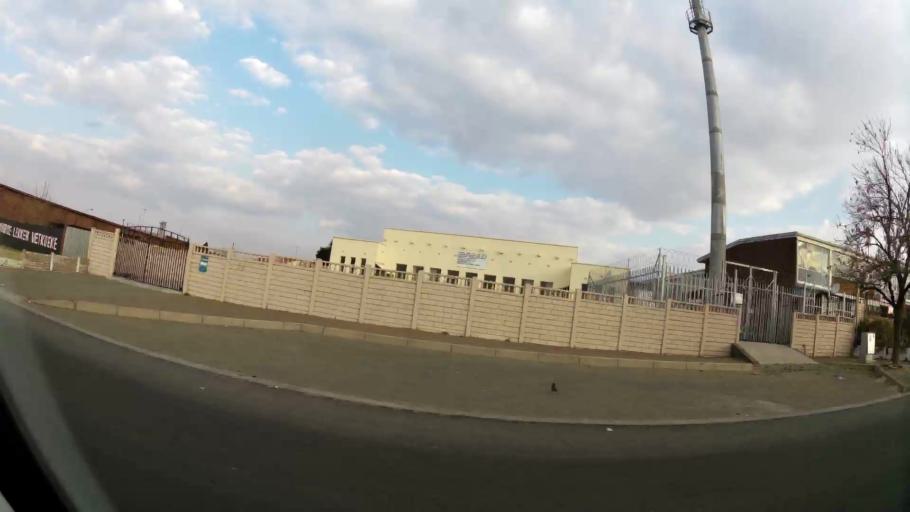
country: ZA
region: Gauteng
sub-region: Ekurhuleni Metropolitan Municipality
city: Germiston
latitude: -26.2362
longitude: 28.1986
